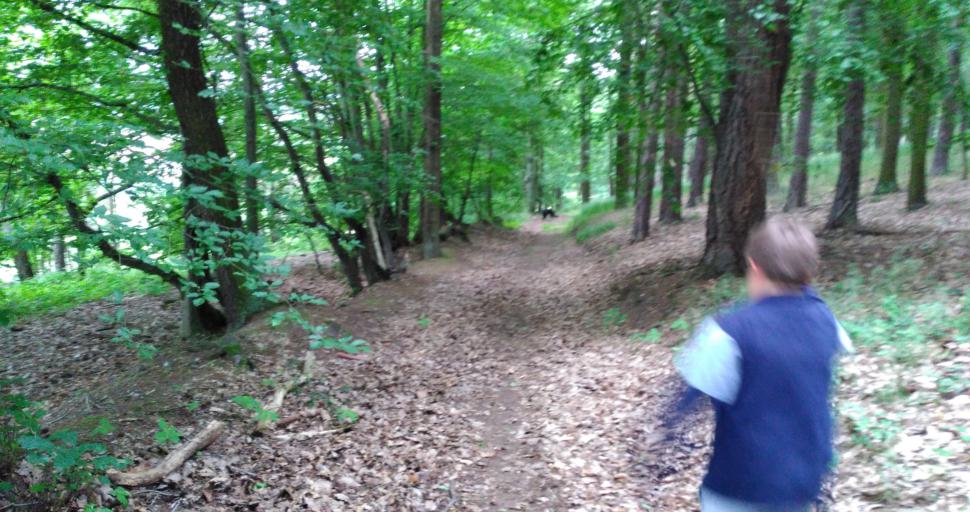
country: CZ
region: Central Bohemia
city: Jince
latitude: 49.7847
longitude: 13.9990
